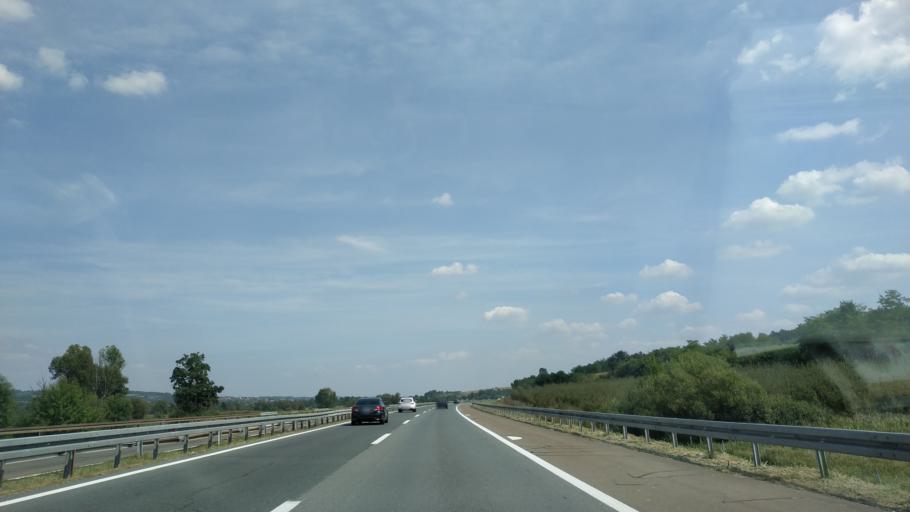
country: RS
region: Central Serbia
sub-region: Belgrade
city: Grocka
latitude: 44.5696
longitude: 20.7036
